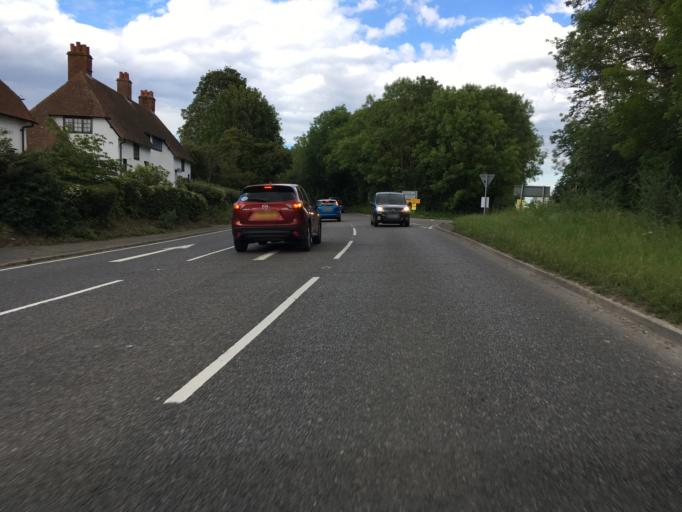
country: GB
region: England
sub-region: Oxfordshire
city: Thame
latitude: 51.7624
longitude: -0.9657
